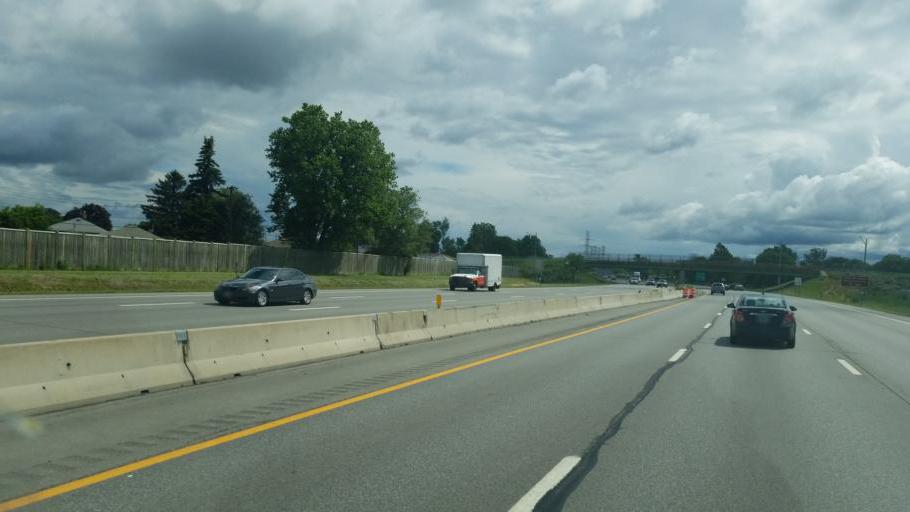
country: US
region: New York
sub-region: Erie County
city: Sloan
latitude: 42.8783
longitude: -78.7766
